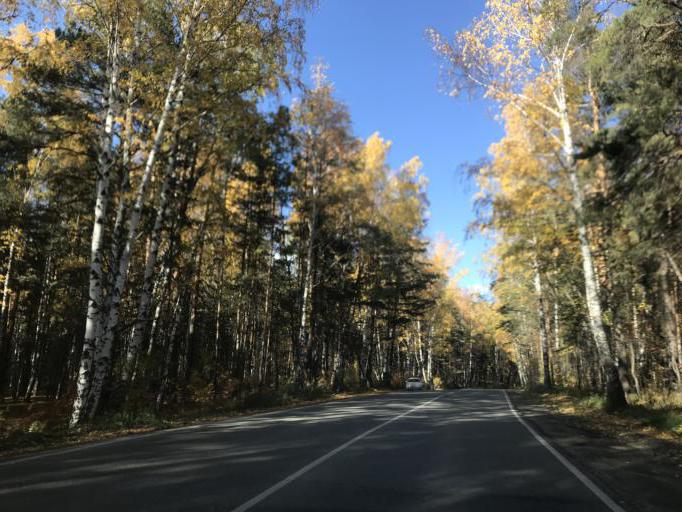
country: RU
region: Chelyabinsk
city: Dolgoderevenskoye
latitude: 55.2901
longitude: 61.3562
